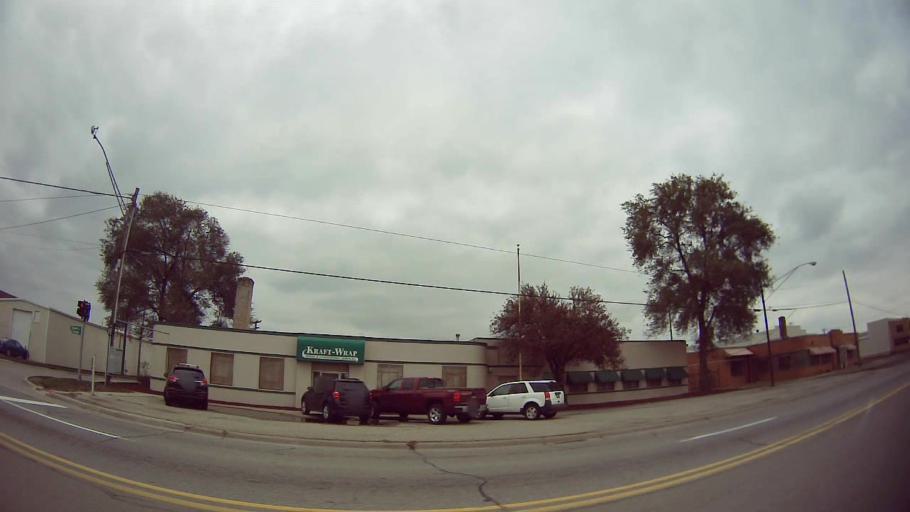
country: US
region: Michigan
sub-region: Macomb County
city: Warren
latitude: 42.4557
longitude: -83.0054
